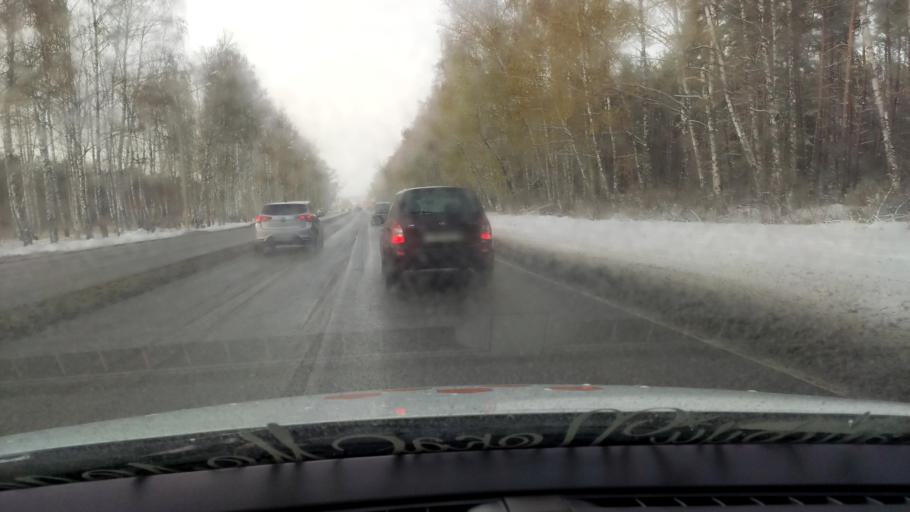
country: RU
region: Voronezj
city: Pridonskoy
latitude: 51.6933
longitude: 39.0944
